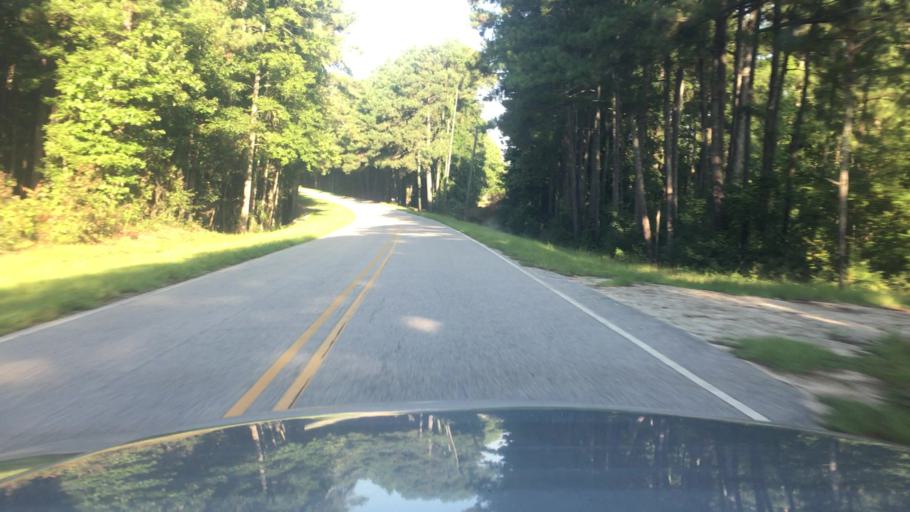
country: US
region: North Carolina
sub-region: Harnett County
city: Walkertown
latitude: 35.2269
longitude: -78.8841
